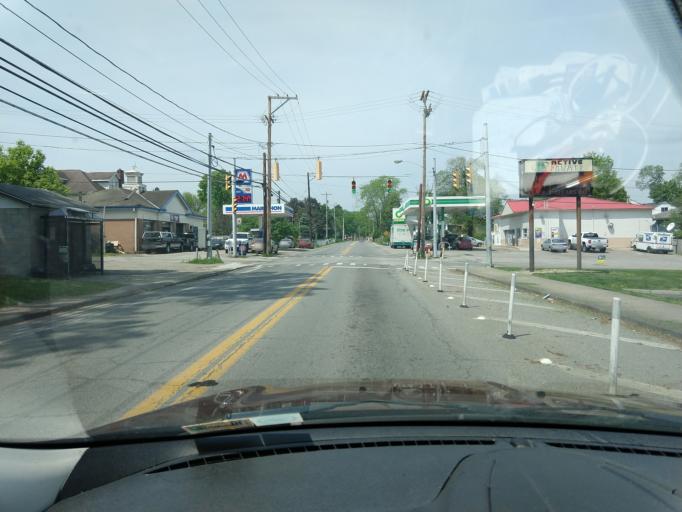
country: US
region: West Virginia
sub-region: Kanawha County
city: Saint Albans
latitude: 38.3772
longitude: -81.8067
